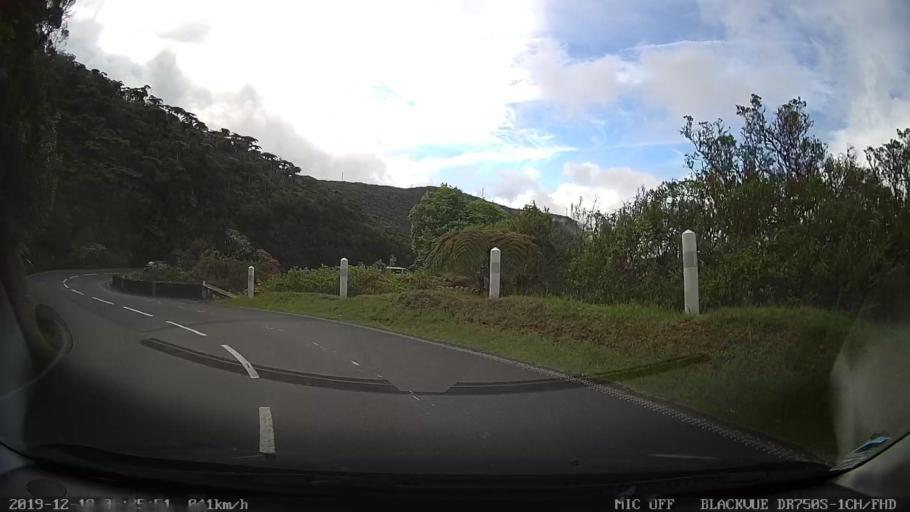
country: RE
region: Reunion
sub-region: Reunion
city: Cilaos
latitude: -21.1624
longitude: 55.5949
